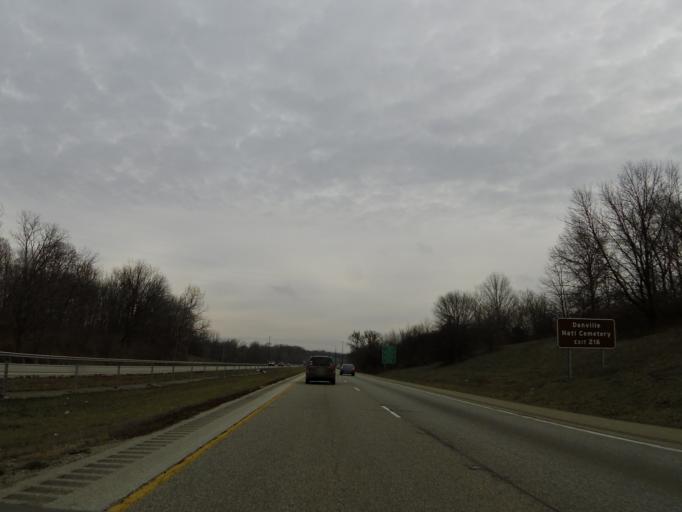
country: US
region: Illinois
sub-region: Vermilion County
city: Danville
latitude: 40.1091
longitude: -87.6191
